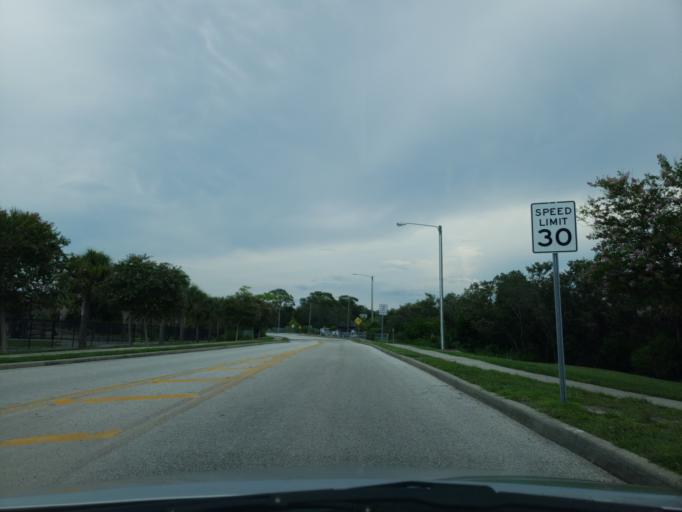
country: US
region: Florida
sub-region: Pinellas County
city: Tarpon Springs
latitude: 28.1541
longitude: -82.7540
